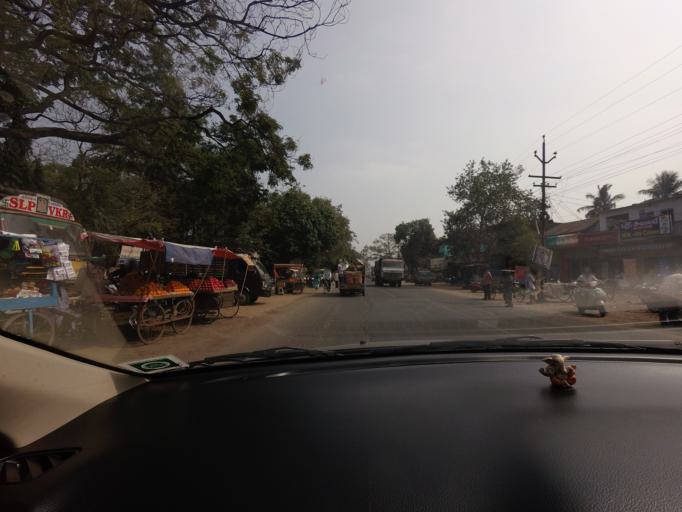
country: IN
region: Andhra Pradesh
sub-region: Krishna
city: Kankipadu
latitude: 16.4360
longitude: 80.7662
